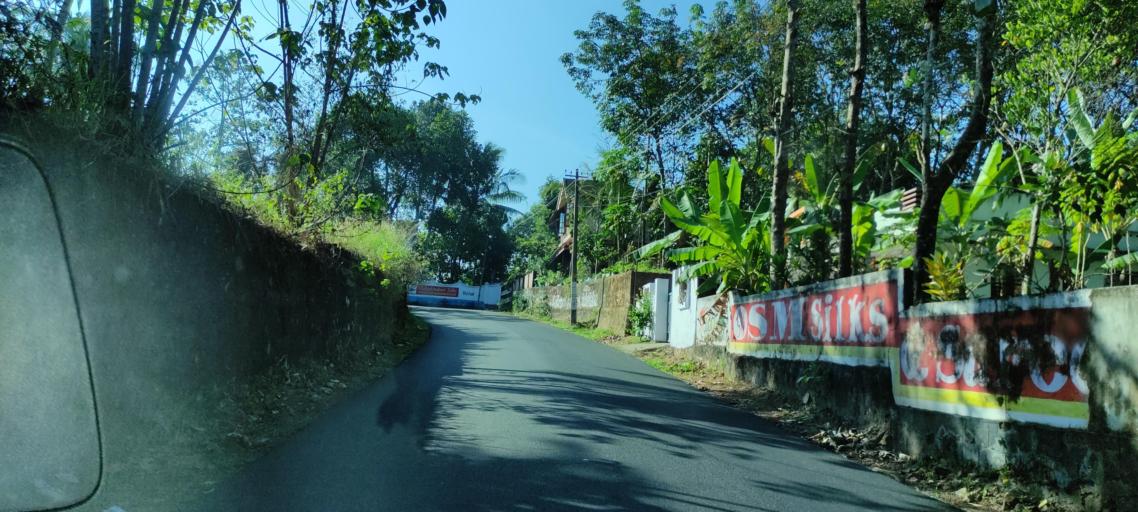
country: IN
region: Kerala
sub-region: Pattanamtitta
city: Adur
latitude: 9.1592
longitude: 76.7148
